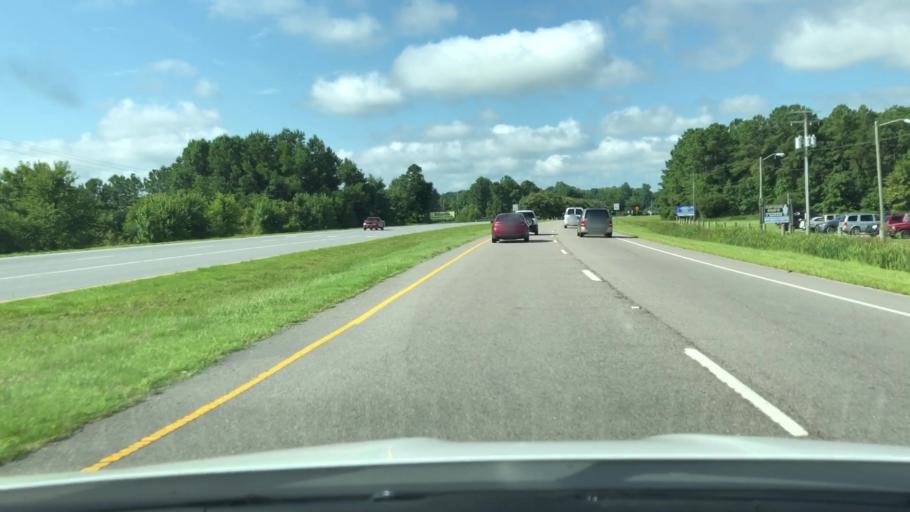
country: US
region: North Carolina
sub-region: Perquimans County
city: Hertford
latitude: 36.1749
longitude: -76.4634
